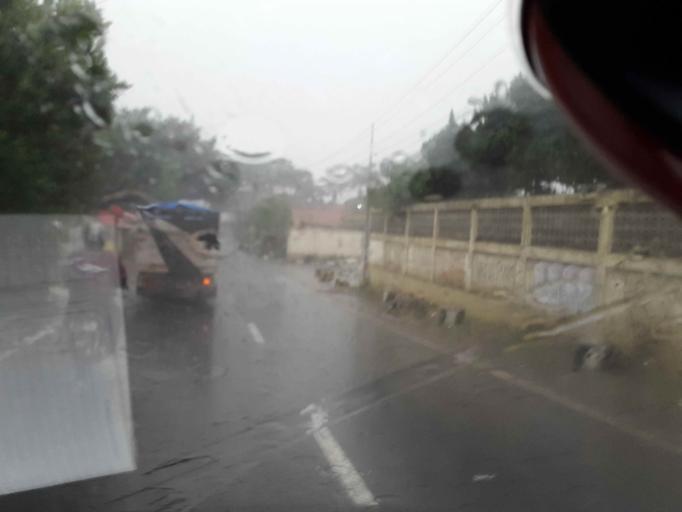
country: ID
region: West Java
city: Cimahi
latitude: -6.8727
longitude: 107.5040
